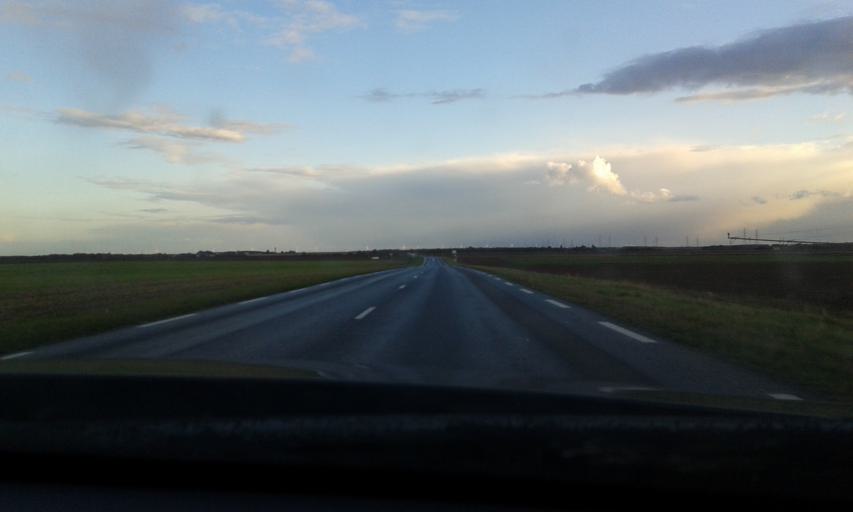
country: FR
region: Centre
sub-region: Departement d'Eure-et-Loir
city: Janville
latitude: 48.2419
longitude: 1.7784
